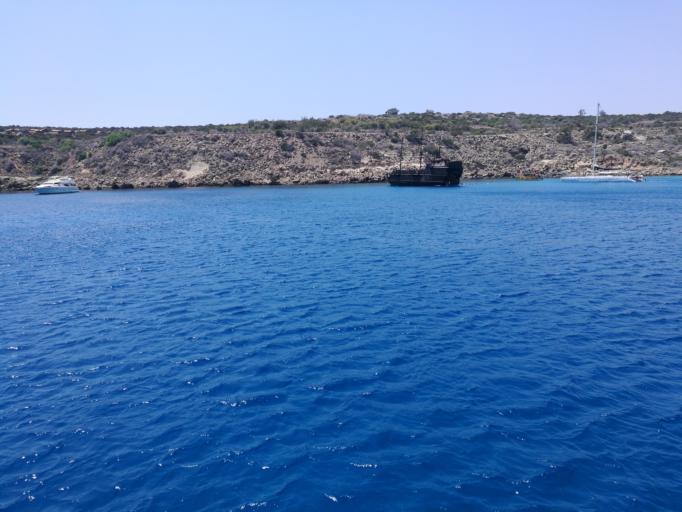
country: CY
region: Ammochostos
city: Protaras
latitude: 34.9785
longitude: 34.0748
